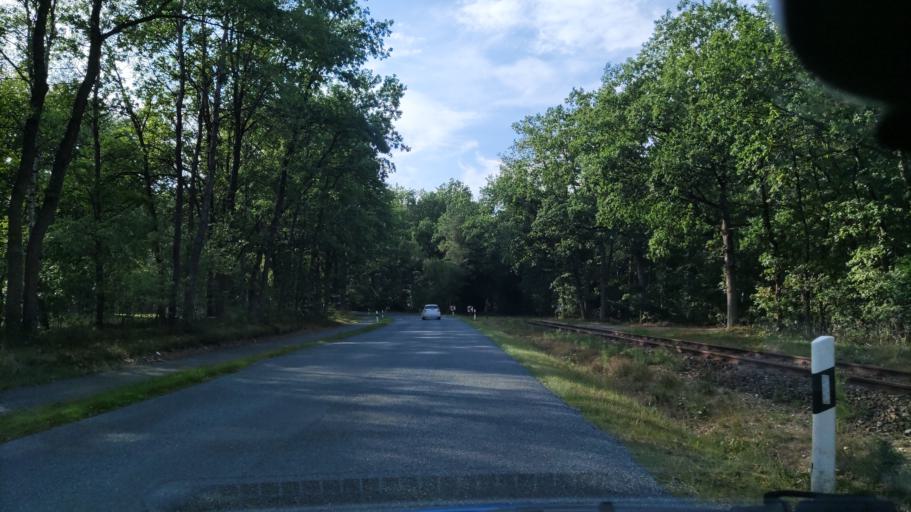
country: DE
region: Lower Saxony
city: Munster
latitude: 52.9877
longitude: 10.1203
